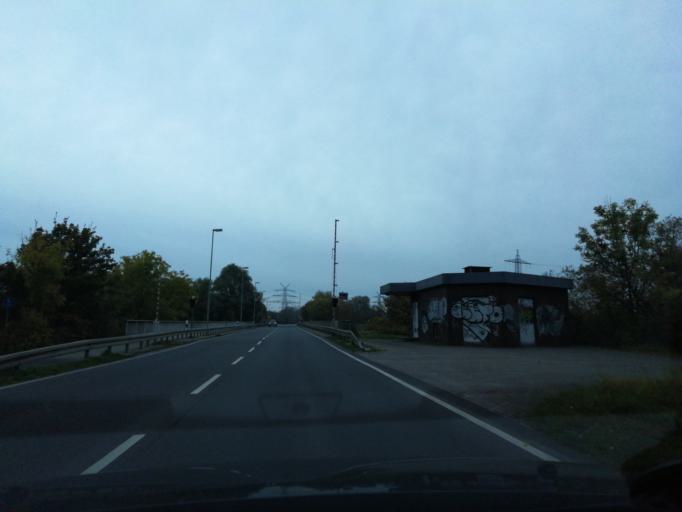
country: DE
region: Lower Saxony
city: Wilhelmshaven
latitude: 53.5585
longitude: 8.1179
